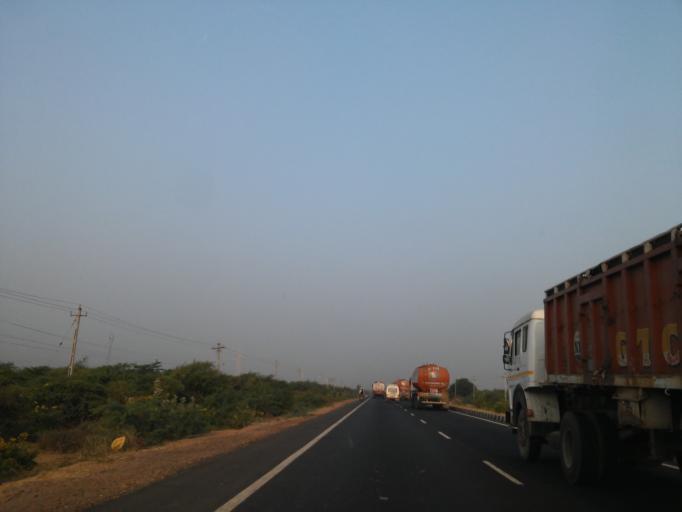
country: IN
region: Gujarat
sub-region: Kachchh
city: Bhachau
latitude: 23.2922
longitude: 70.5752
